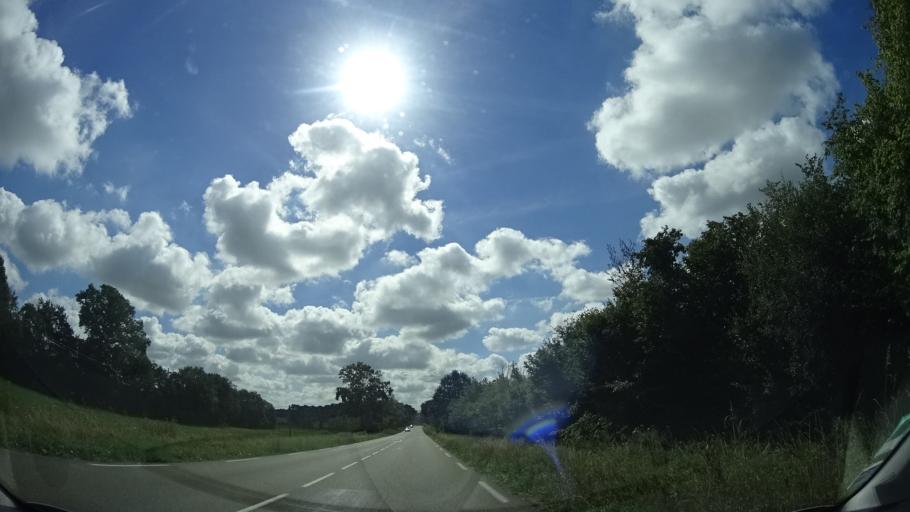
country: FR
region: Pays de la Loire
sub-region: Departement de la Mayenne
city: Entrammes
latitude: 48.0119
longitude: -0.6661
